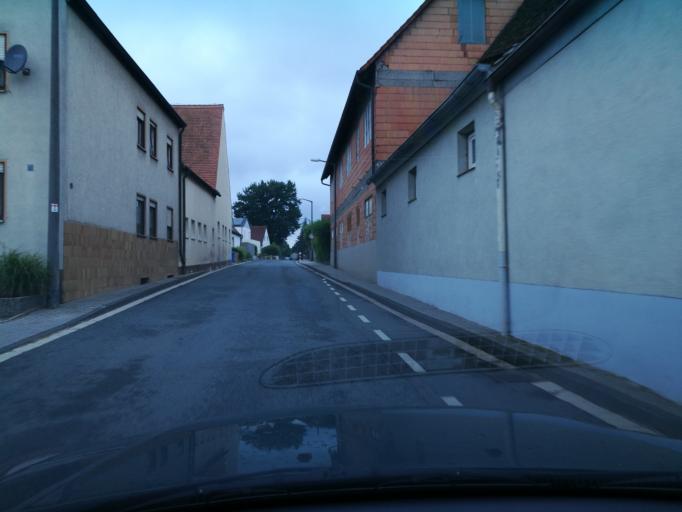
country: DE
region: Bavaria
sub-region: Regierungsbezirk Mittelfranken
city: Obermichelbach
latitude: 49.5407
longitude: 10.9615
